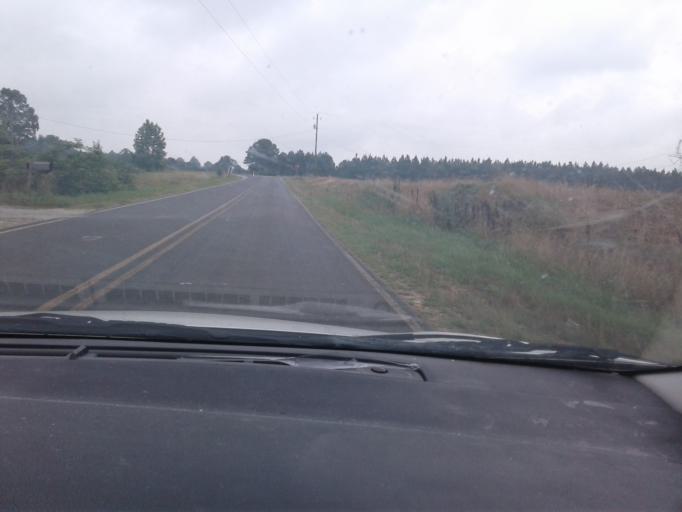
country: US
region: North Carolina
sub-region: Harnett County
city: Coats
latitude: 35.3750
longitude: -78.6474
